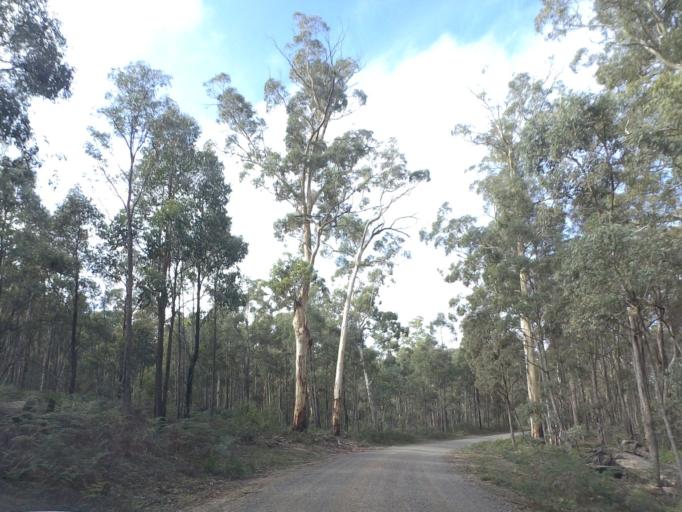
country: AU
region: Victoria
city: Brown Hill
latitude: -37.4941
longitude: 144.1763
